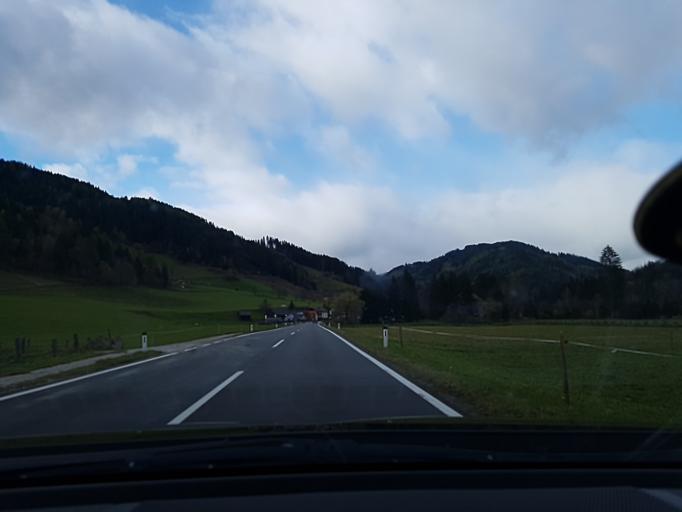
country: AT
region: Styria
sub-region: Politischer Bezirk Murtal
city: Oberzeiring
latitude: 47.2726
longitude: 14.4847
